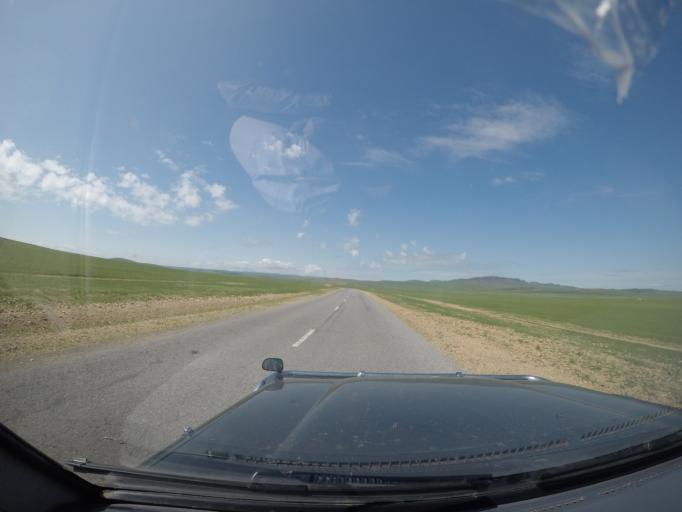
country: MN
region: Hentiy
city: Dundburd
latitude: 47.3450
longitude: 111.4949
